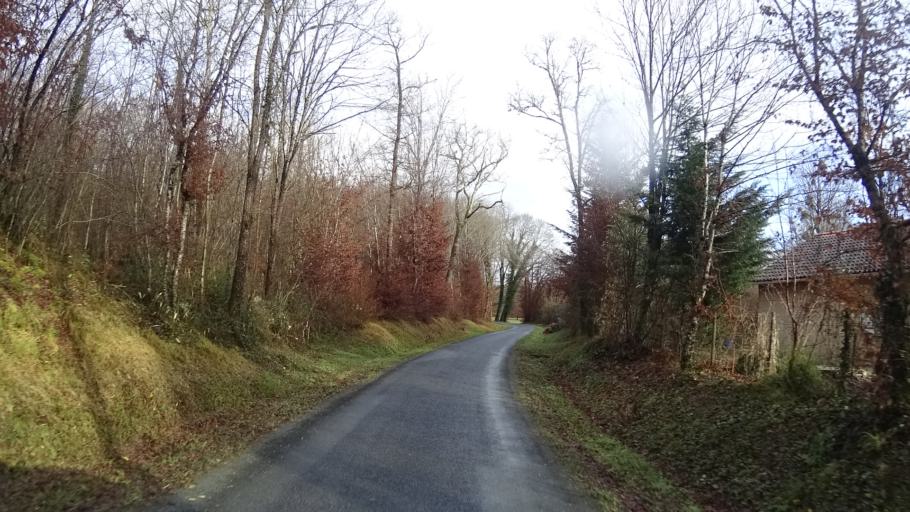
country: FR
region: Aquitaine
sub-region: Departement de la Dordogne
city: Thiviers
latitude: 45.3607
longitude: 0.9527
